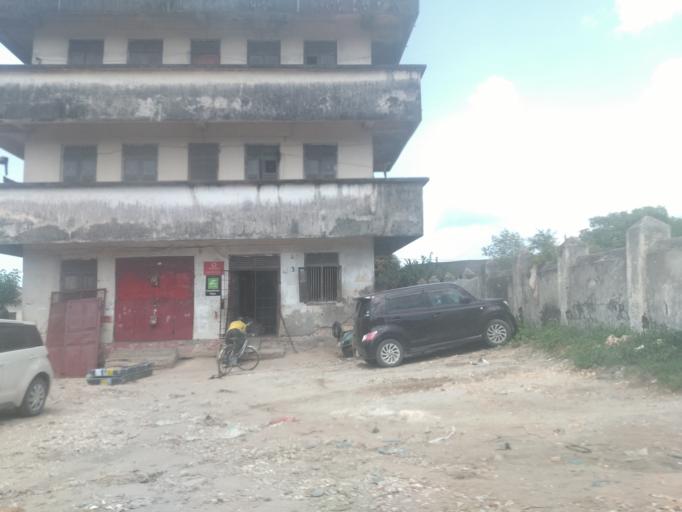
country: TZ
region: Zanzibar Urban/West
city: Zanzibar
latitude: -6.1536
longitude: 39.2083
